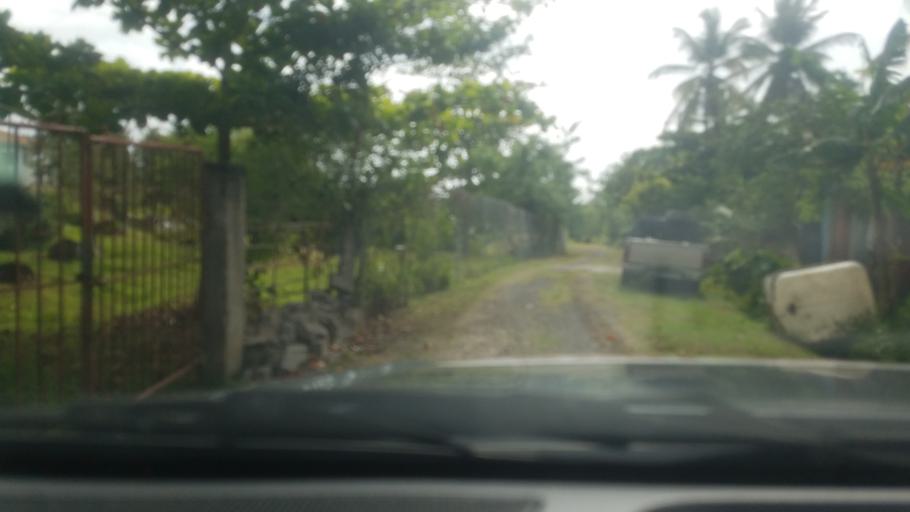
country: LC
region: Micoud Quarter
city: Micoud
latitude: 13.7996
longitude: -60.9198
